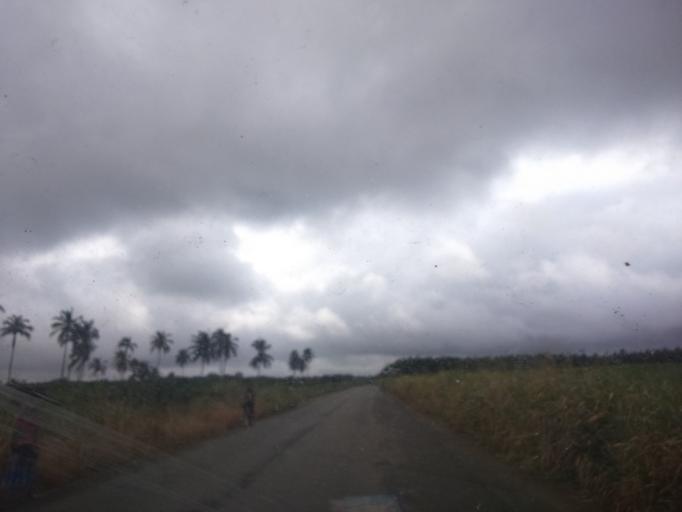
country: CI
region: Sud-Comoe
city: Adiake
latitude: 5.2957
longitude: -3.4307
